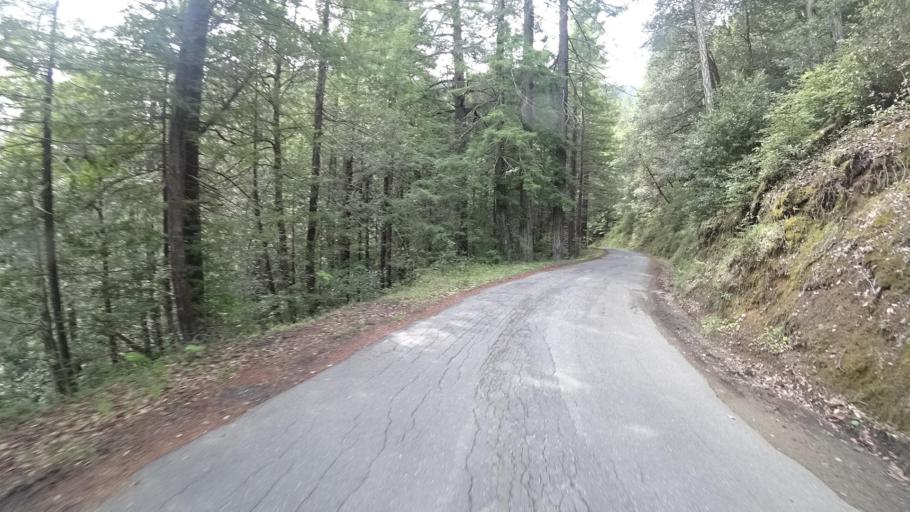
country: US
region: California
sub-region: Humboldt County
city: Redway
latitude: 40.3388
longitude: -123.8677
